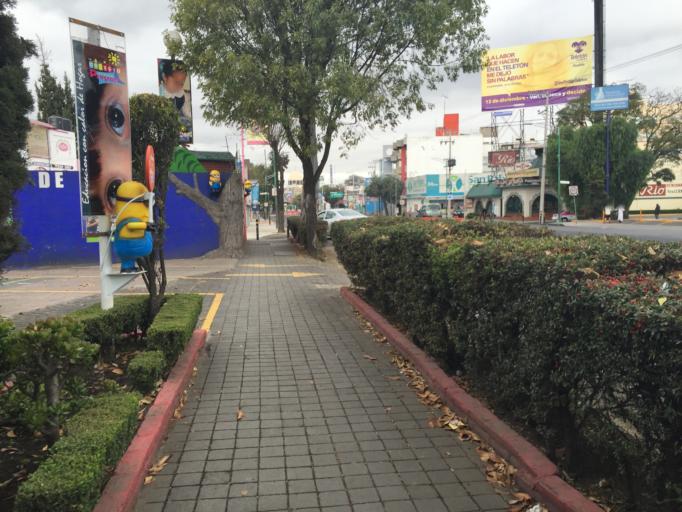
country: MX
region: Mexico
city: Colonia Lindavista
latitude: 19.4876
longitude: -99.1253
